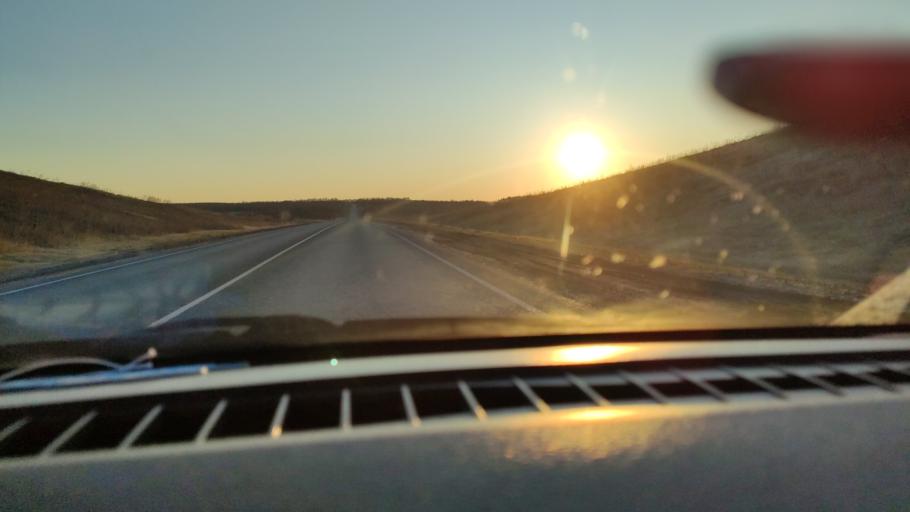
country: RU
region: Saratov
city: Sinodskoye
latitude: 51.9284
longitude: 46.5726
